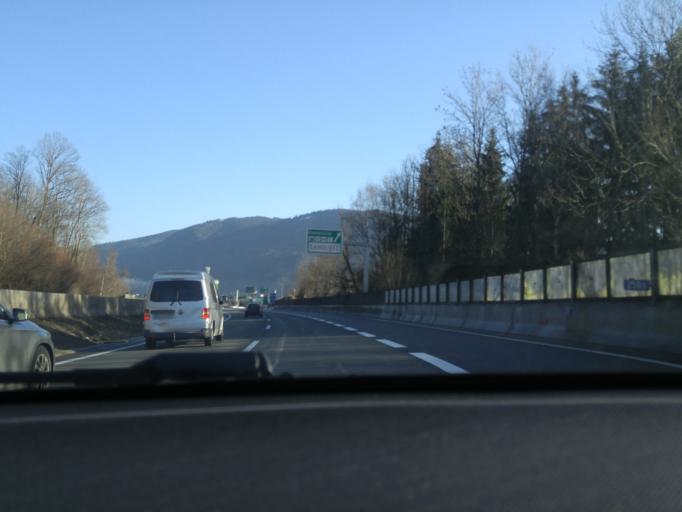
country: AT
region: Upper Austria
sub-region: Politischer Bezirk Vocklabruck
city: Innerschwand
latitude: 47.8382
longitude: 13.3905
